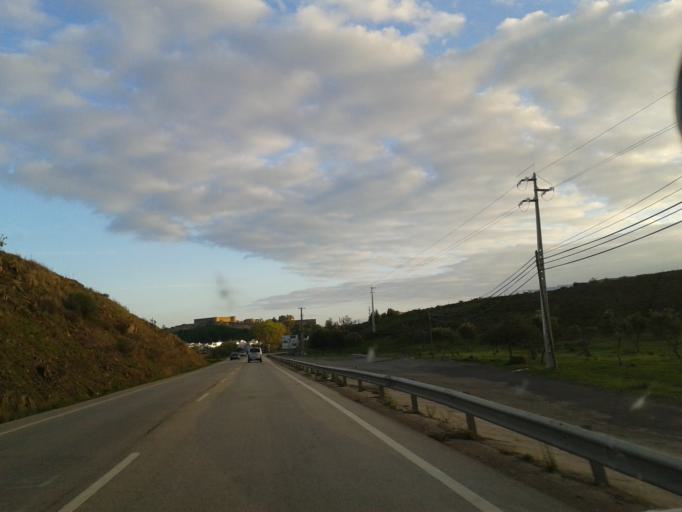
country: PT
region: Faro
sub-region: Castro Marim
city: Castro Marim
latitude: 37.2257
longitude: -7.4463
